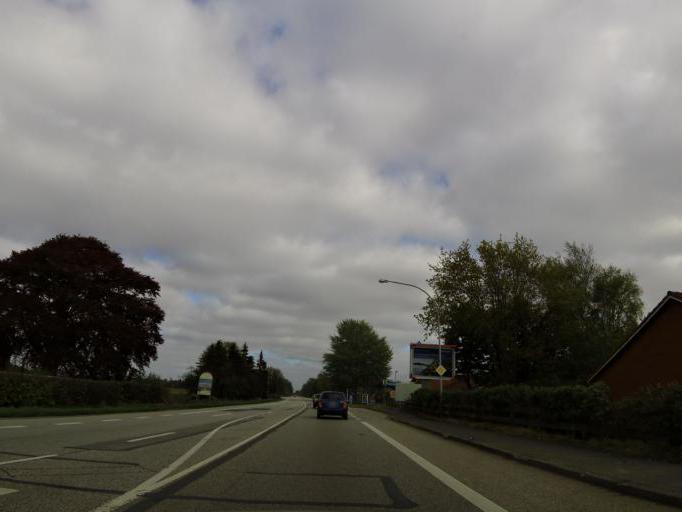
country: DE
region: Schleswig-Holstein
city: Risum-Lindholm
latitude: 54.7614
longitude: 8.8760
